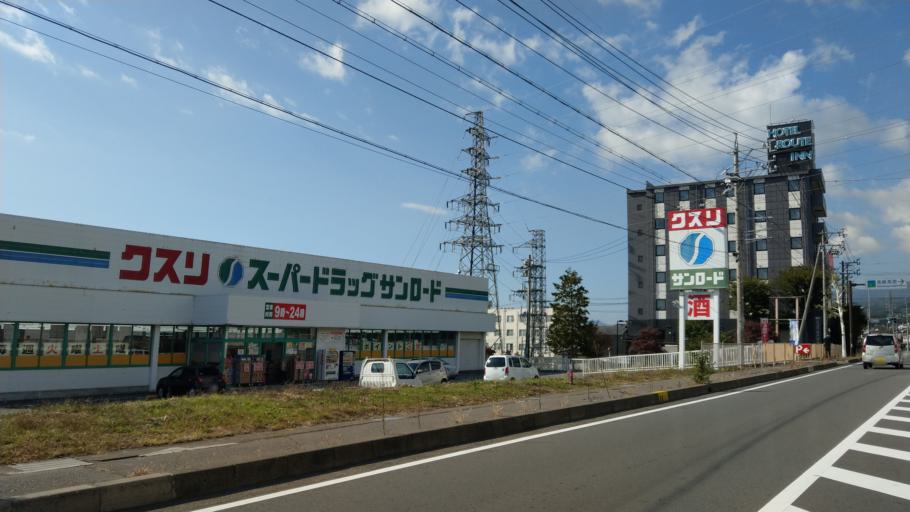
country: JP
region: Nagano
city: Komoro
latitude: 36.3280
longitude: 138.4339
